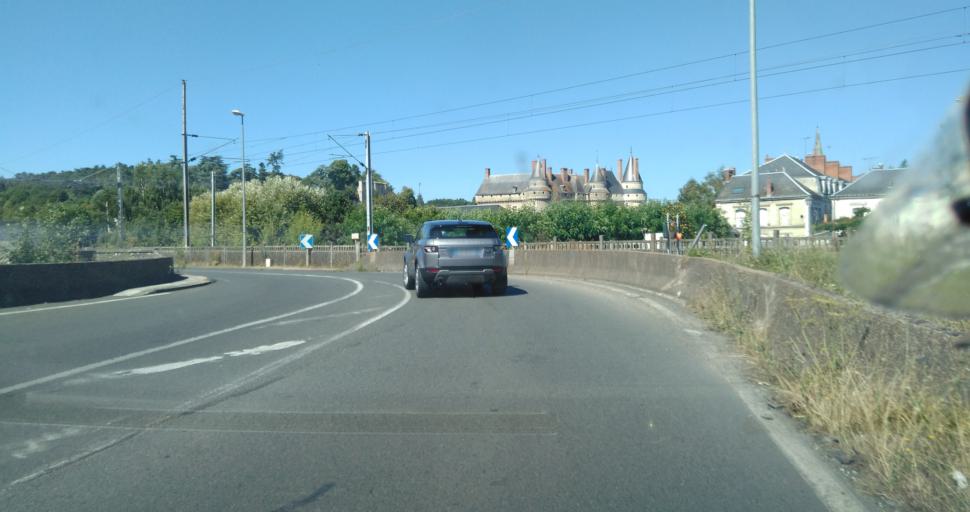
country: FR
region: Centre
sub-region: Departement d'Indre-et-Loire
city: Langeais
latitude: 47.3236
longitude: 0.4101
